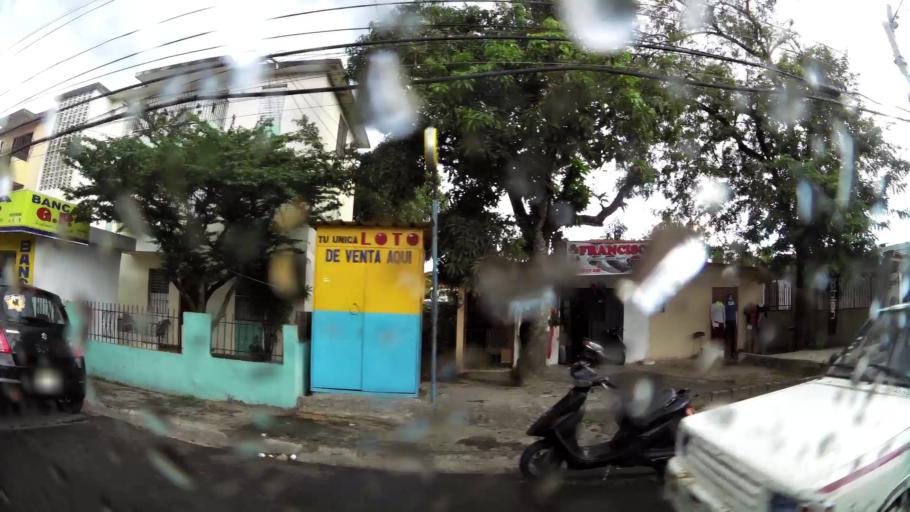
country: DO
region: Monsenor Nouel
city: Bonao
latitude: 18.9344
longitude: -70.4090
